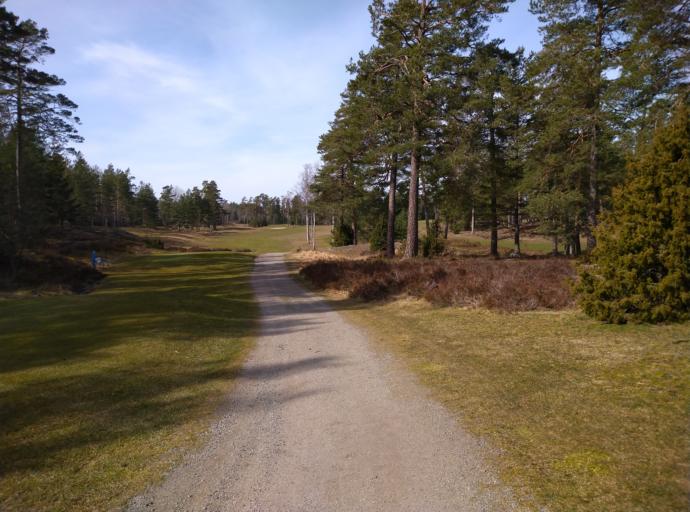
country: SE
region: Stockholm
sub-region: Nacka Kommun
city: Fisksatra
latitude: 59.2862
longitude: 18.2473
